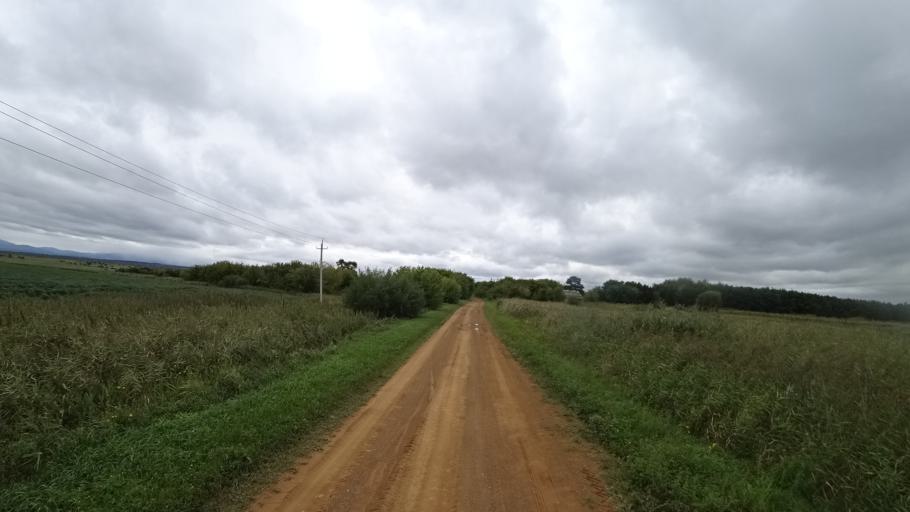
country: RU
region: Primorskiy
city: Chernigovka
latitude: 44.4347
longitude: 132.5923
